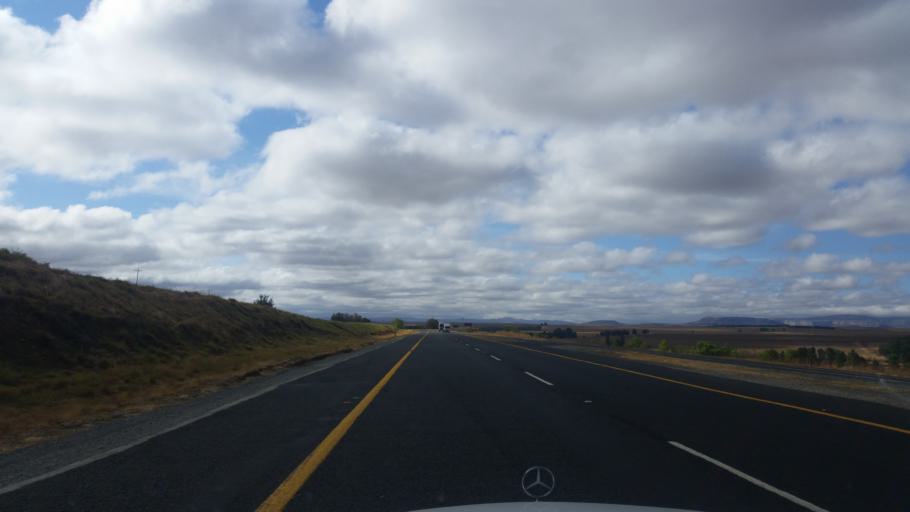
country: ZA
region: Orange Free State
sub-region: Thabo Mofutsanyana District Municipality
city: Phuthaditjhaba
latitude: -28.3084
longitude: 28.7122
